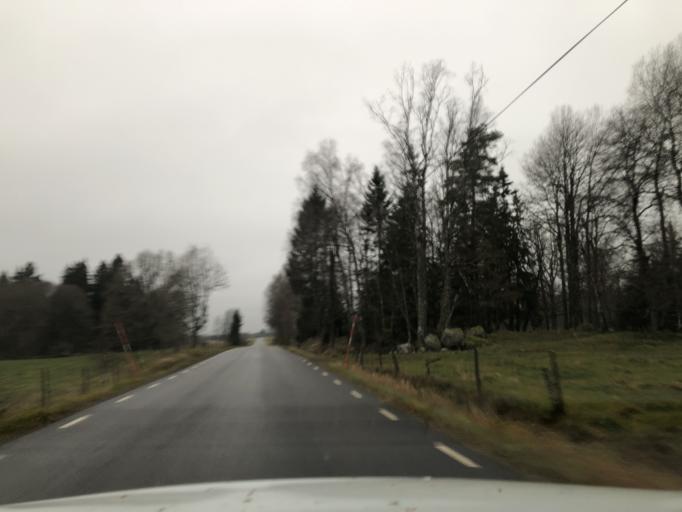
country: SE
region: Vaestra Goetaland
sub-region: Ulricehamns Kommun
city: Ulricehamn
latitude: 57.8378
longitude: 13.3822
